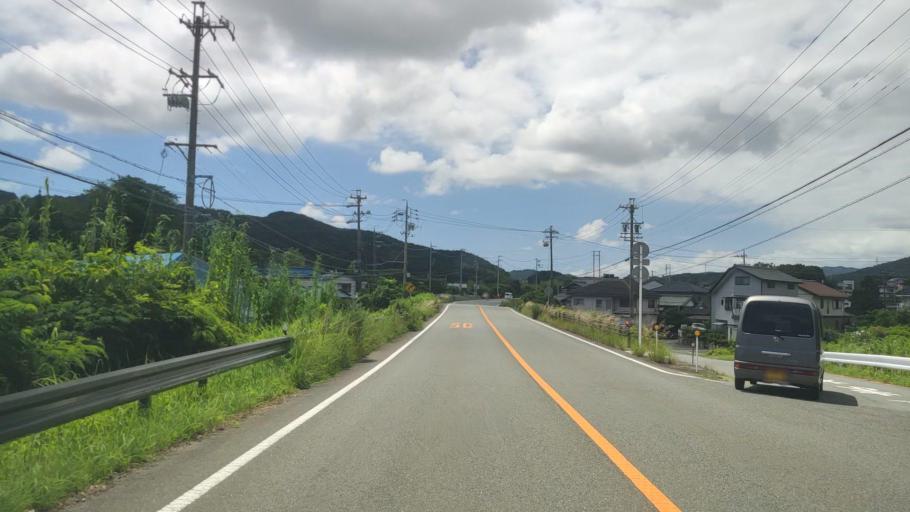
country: JP
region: Mie
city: Toba
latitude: 34.4593
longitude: 136.8422
